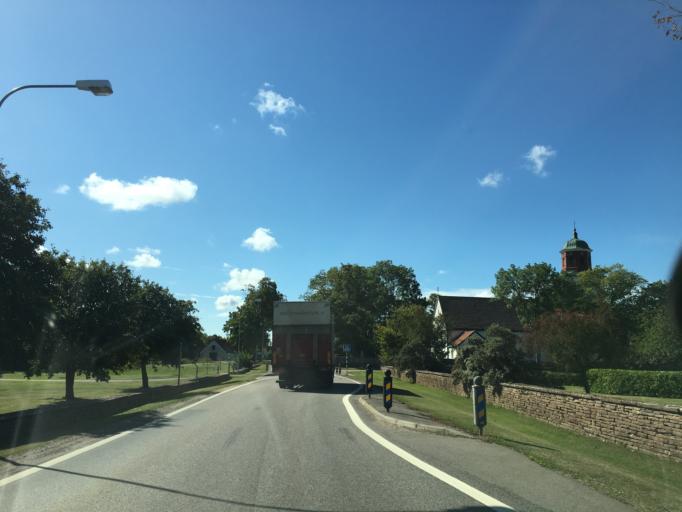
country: SE
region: Kalmar
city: Faerjestaden
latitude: 56.6345
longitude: 16.5161
